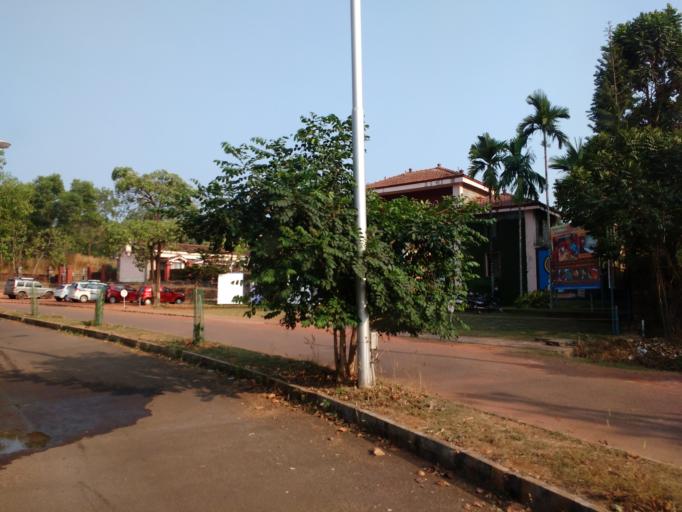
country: IN
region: Karnataka
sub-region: Dakshina Kannada
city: Mangalore
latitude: 12.9276
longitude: 74.8965
